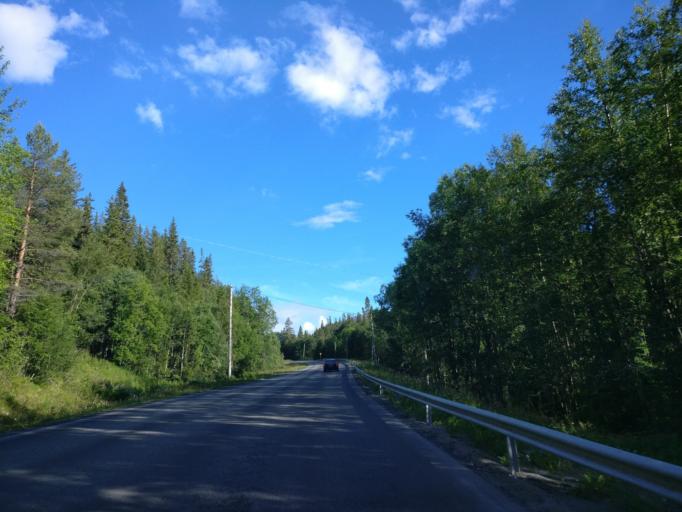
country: SE
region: Jaemtland
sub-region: Bergs Kommun
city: Hoverberg
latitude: 62.4877
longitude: 13.9640
